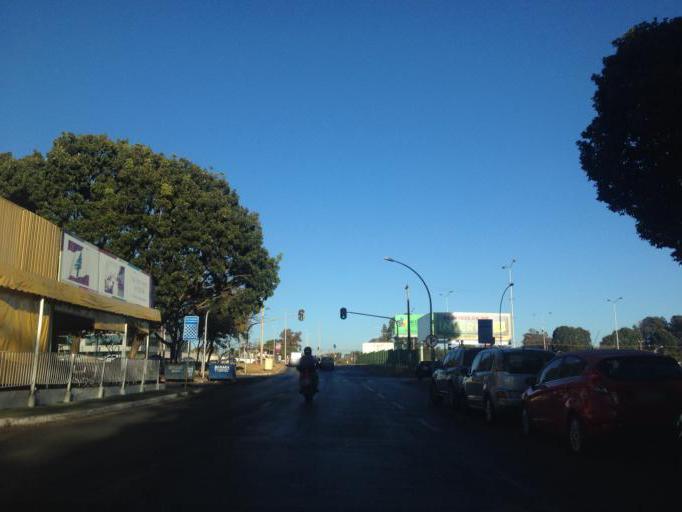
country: BR
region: Federal District
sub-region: Brasilia
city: Brasilia
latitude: -15.7694
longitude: -47.8918
